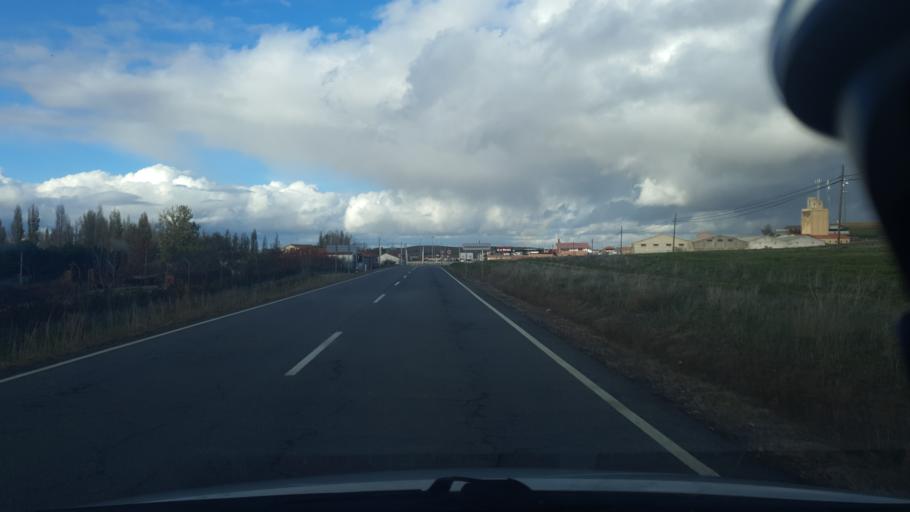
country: ES
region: Castille and Leon
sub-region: Provincia de Avila
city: Hernansancho
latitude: 40.8517
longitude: -4.7303
